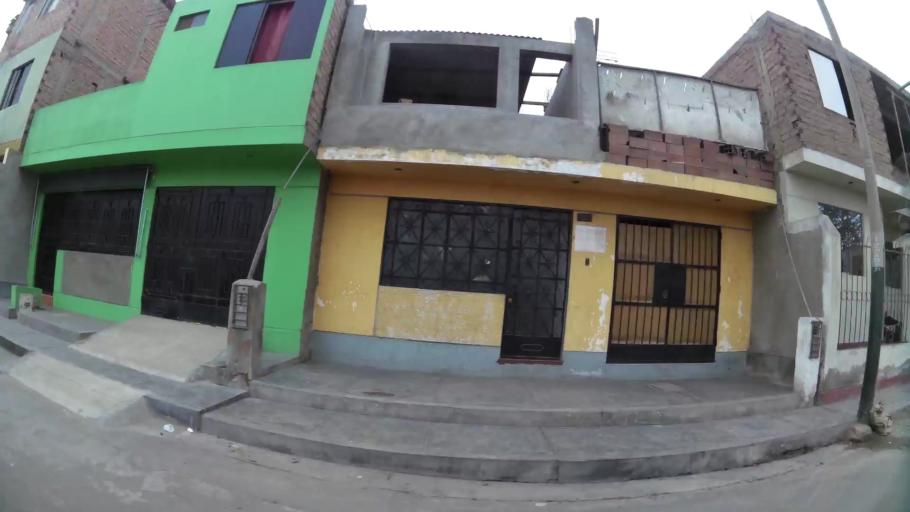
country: PE
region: Lima
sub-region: Lima
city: Surco
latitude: -12.1743
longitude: -76.9638
